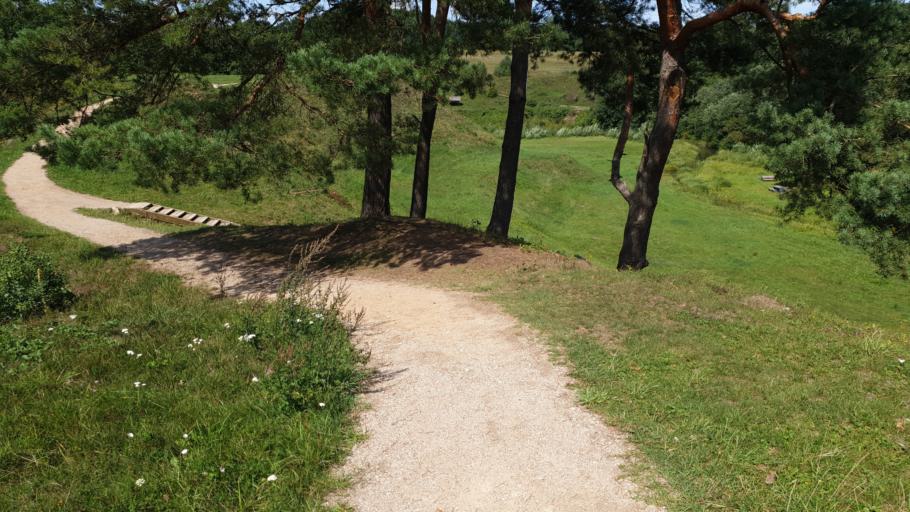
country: LT
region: Vilnius County
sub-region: Vilniaus Rajonas
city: Vievis
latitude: 54.8244
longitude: 24.9445
